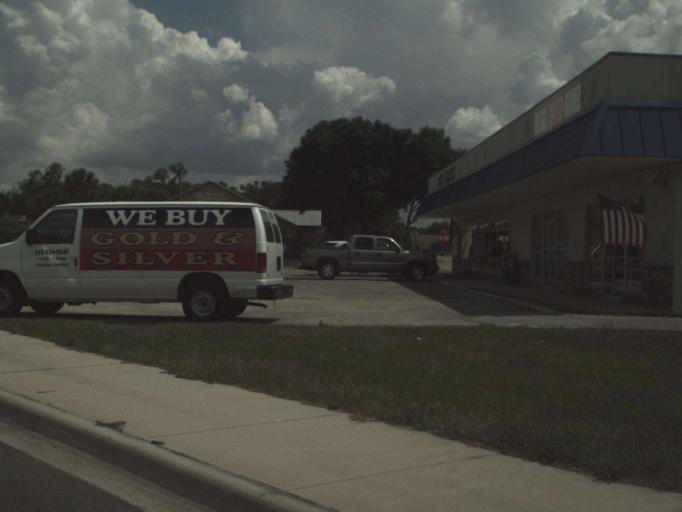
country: US
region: Florida
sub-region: Lake County
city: Leesburg
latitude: 28.8252
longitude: -81.8861
